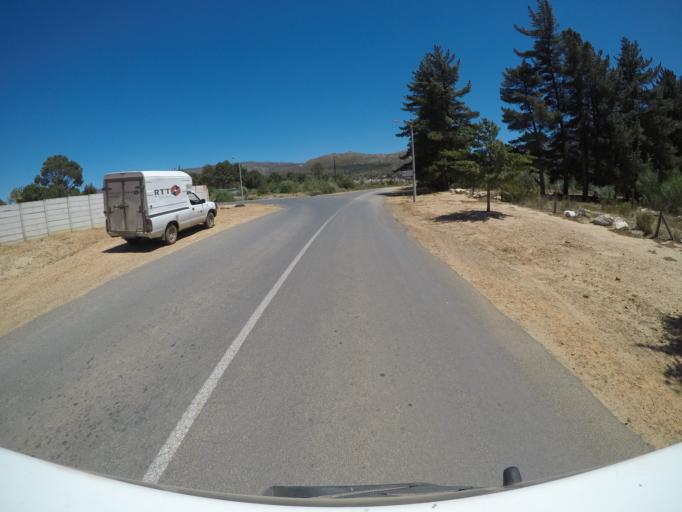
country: ZA
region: Western Cape
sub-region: Overberg District Municipality
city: Hermanus
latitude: -34.2235
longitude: 19.2005
